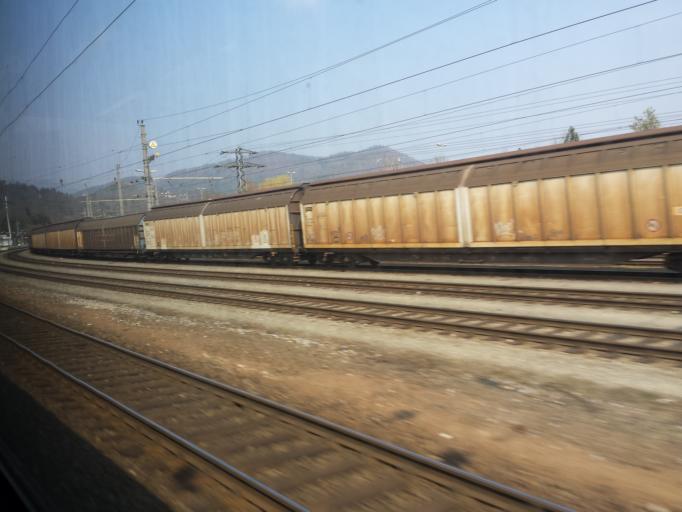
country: AT
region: Styria
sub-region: Politischer Bezirk Graz-Umgebung
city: Gratwein
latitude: 47.1274
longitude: 15.3257
